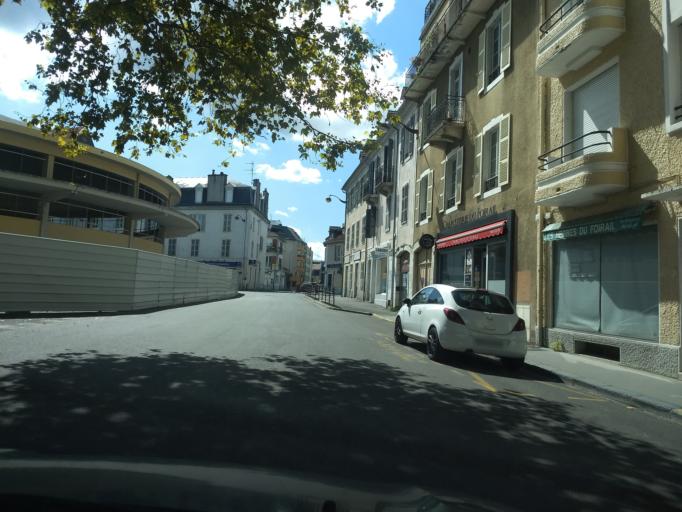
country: FR
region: Aquitaine
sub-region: Departement des Pyrenees-Atlantiques
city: Pau
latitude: 43.3037
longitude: -0.3709
